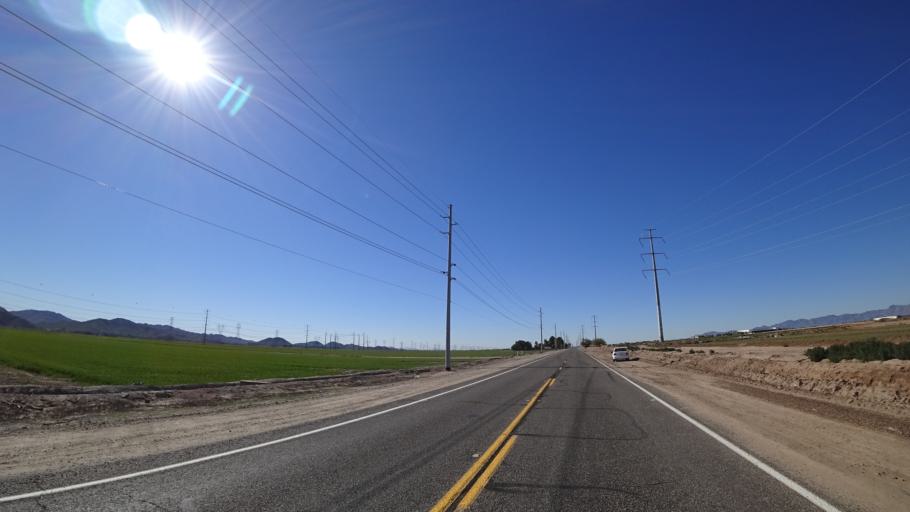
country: US
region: Arizona
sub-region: Maricopa County
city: Goodyear
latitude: 33.4065
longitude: -112.3606
